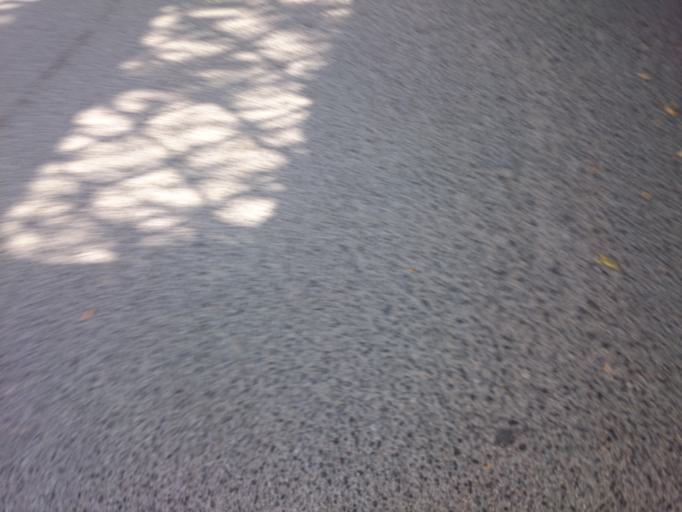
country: ME
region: Kotor
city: Kotor
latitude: 42.4362
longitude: 18.7647
